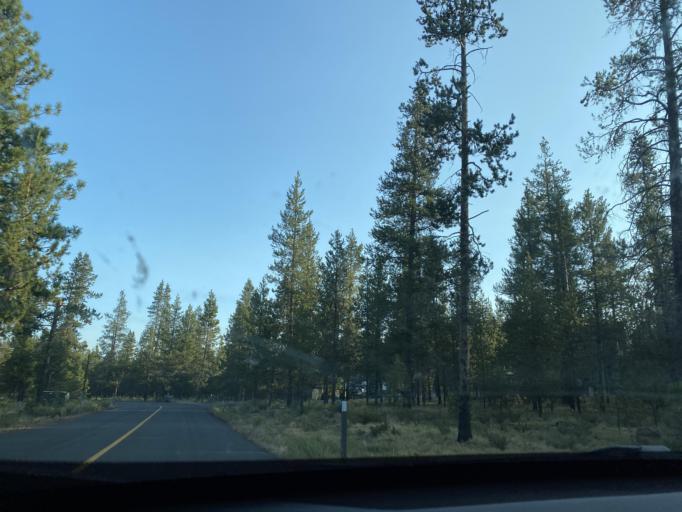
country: US
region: Oregon
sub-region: Deschutes County
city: Sunriver
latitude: 43.8939
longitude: -121.4384
